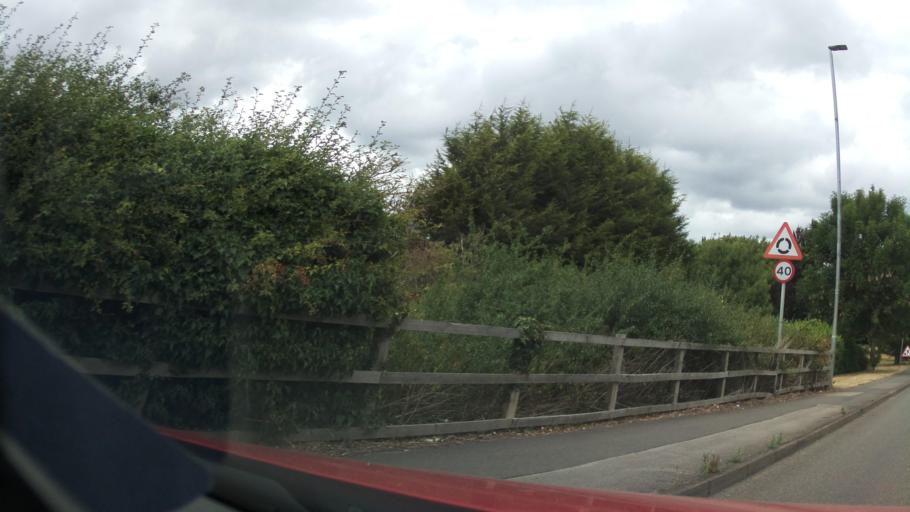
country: GB
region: England
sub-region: Leicestershire
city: Castle Donington
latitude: 52.8534
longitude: -1.3347
